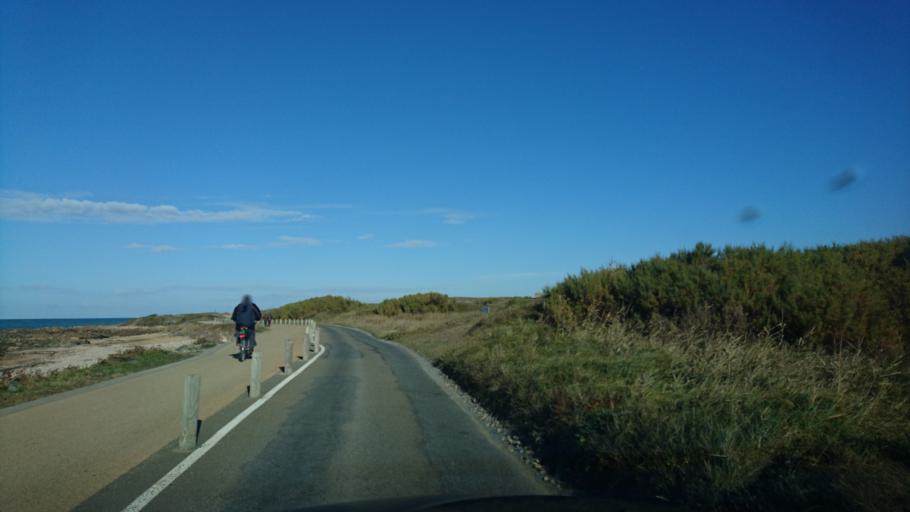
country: FR
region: Pays de la Loire
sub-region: Departement de la Vendee
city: Les Sables-d'Olonne
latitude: 46.5077
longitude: -1.8172
